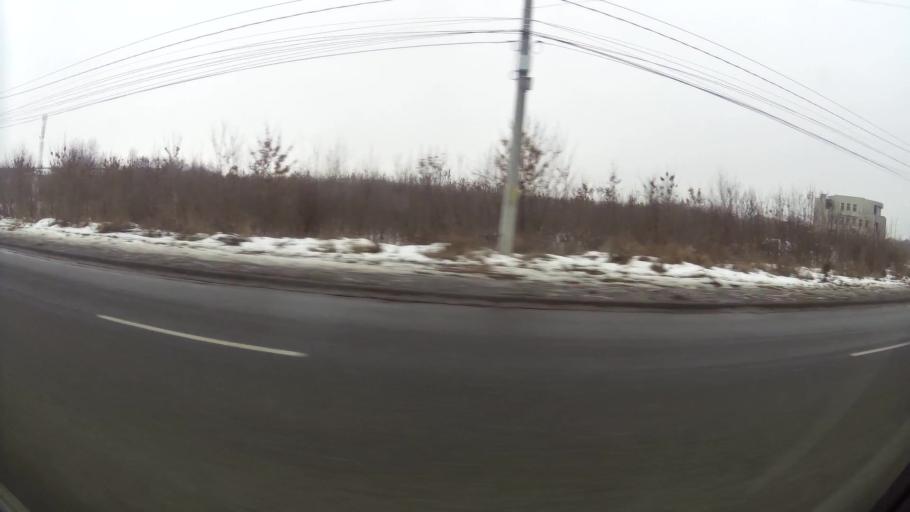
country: RO
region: Ilfov
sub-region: Comuna Magurele
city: Magurele
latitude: 44.3773
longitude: 26.0471
